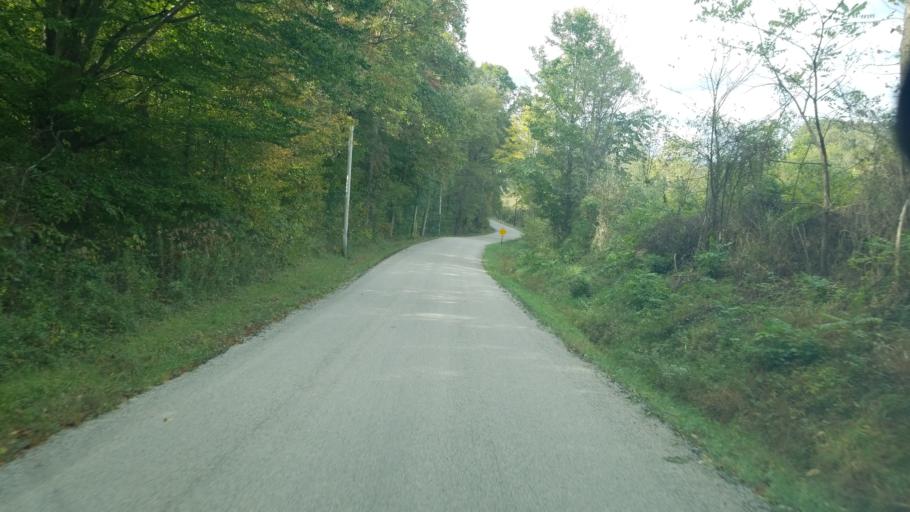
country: US
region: Ohio
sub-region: Vinton County
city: McArthur
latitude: 39.2247
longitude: -82.5090
